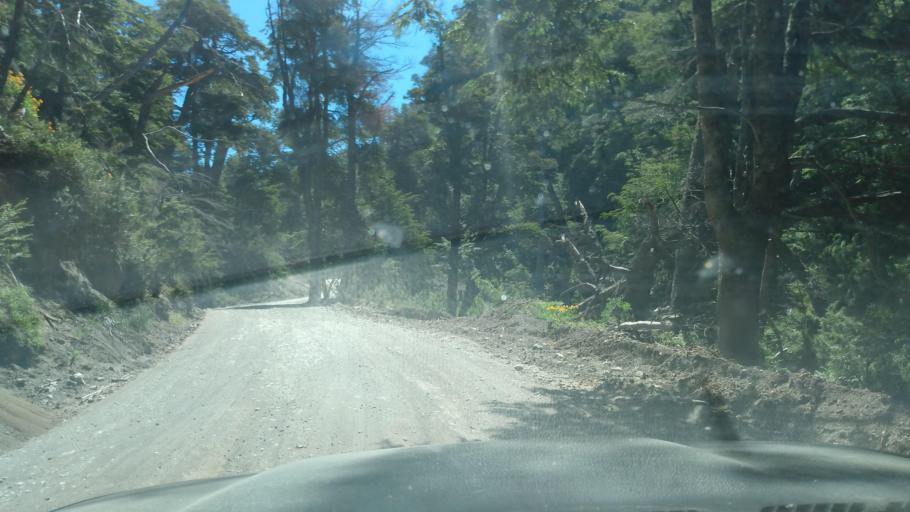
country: AR
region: Neuquen
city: Villa La Angostura
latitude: -40.6031
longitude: -71.6304
